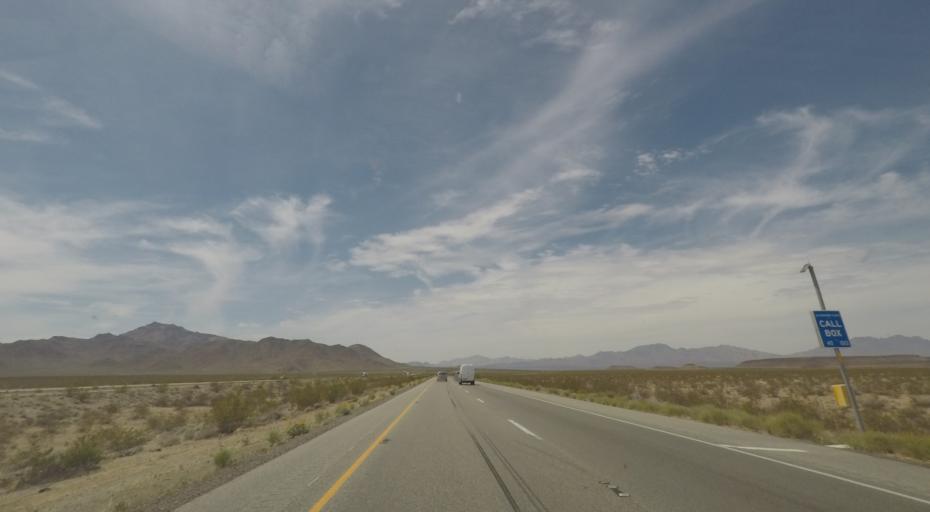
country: US
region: California
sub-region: San Bernardino County
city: Needles
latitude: 34.8029
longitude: -115.2984
